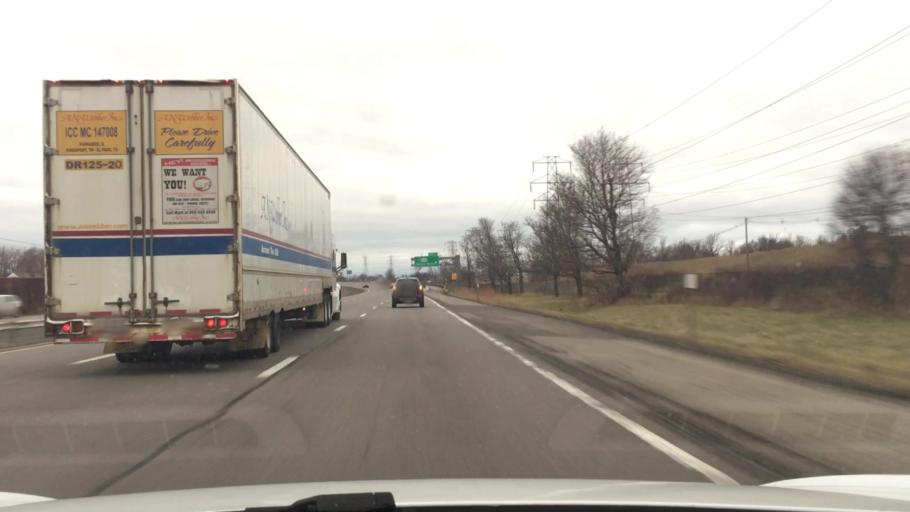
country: US
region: New York
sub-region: Erie County
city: Tonawanda
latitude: 43.0012
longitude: -78.8452
